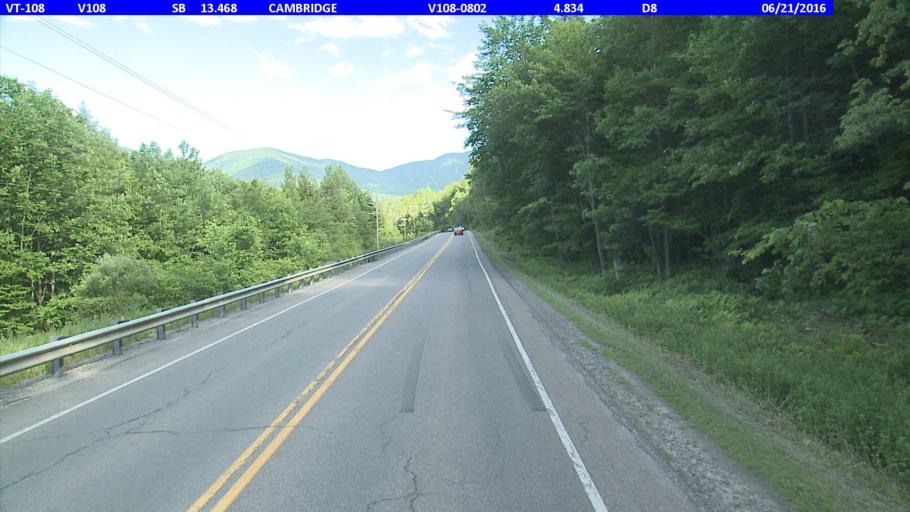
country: US
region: Vermont
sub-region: Lamoille County
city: Johnson
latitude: 44.5959
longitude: -72.8030
